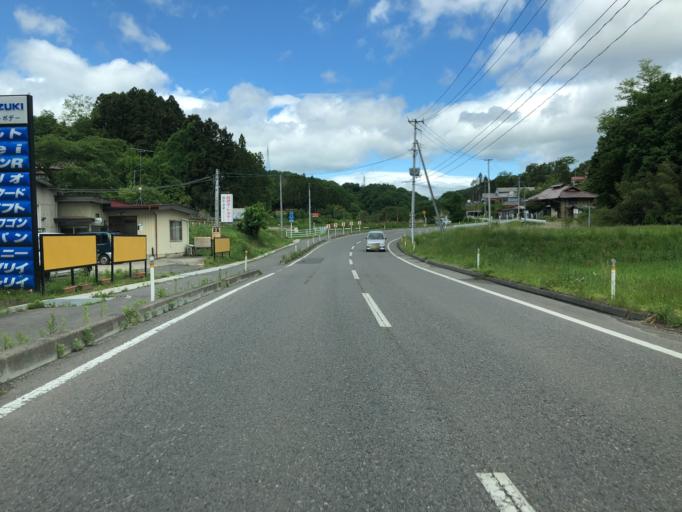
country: JP
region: Fukushima
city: Motomiya
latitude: 37.4956
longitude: 140.4228
